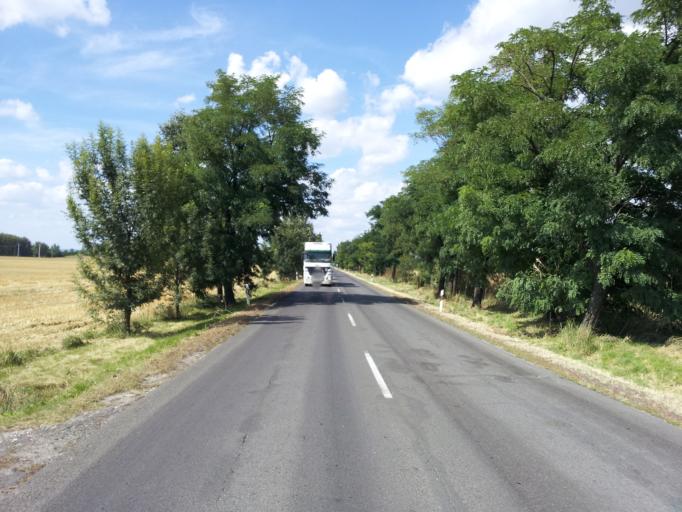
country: HU
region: Pest
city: Dunavarsany
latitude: 47.2533
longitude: 19.0248
